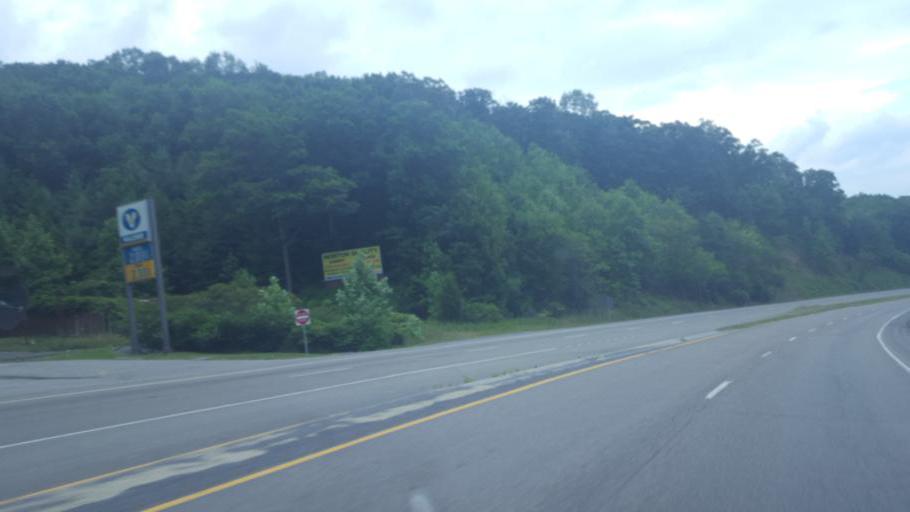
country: US
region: Kentucky
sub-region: Letcher County
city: Jenkins
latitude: 37.1557
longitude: -82.6286
